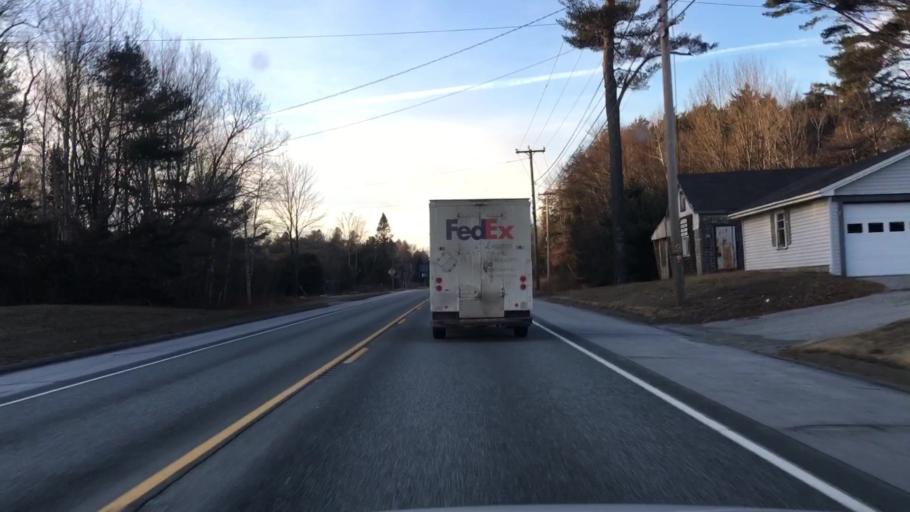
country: US
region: Maine
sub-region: Penobscot County
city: Holden
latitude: 44.7416
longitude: -68.6344
